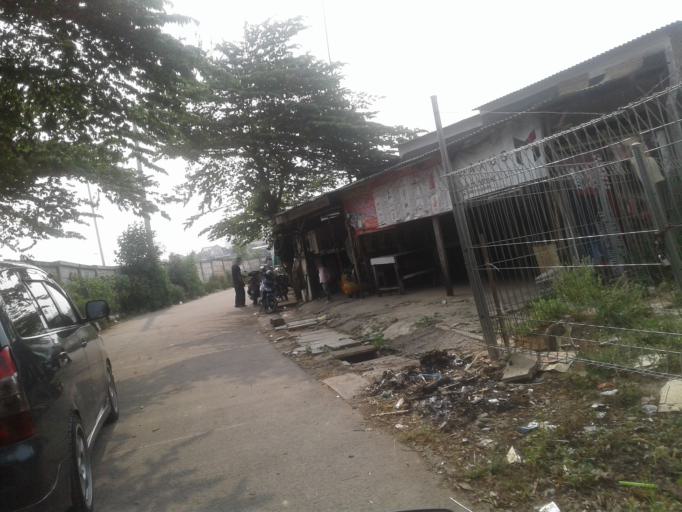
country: ID
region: West Java
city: Depok
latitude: -6.3782
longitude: 106.8379
